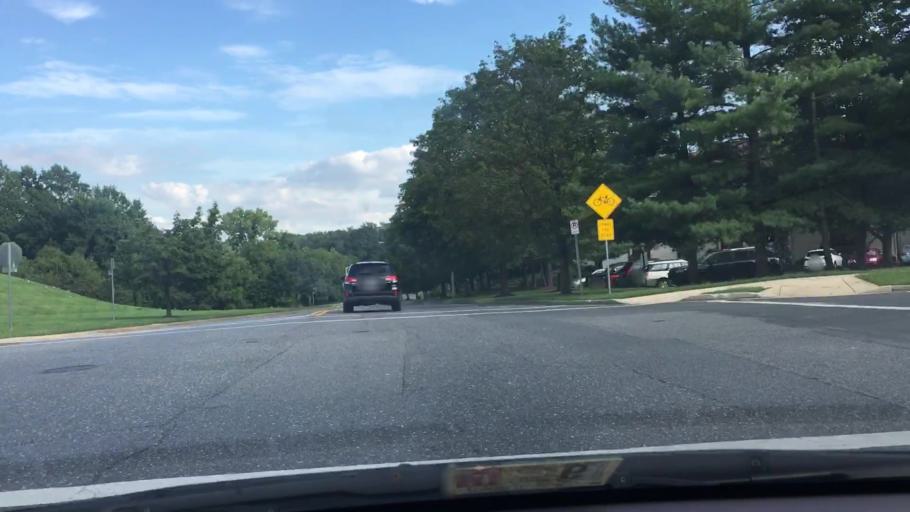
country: US
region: Maryland
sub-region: Montgomery County
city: Olney
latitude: 39.1563
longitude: -77.0587
